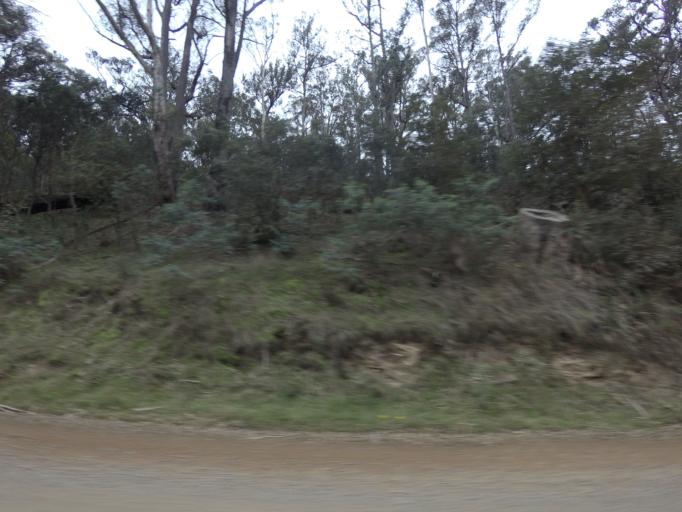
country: AU
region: Tasmania
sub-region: Derwent Valley
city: New Norfolk
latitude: -42.5848
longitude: 147.0111
